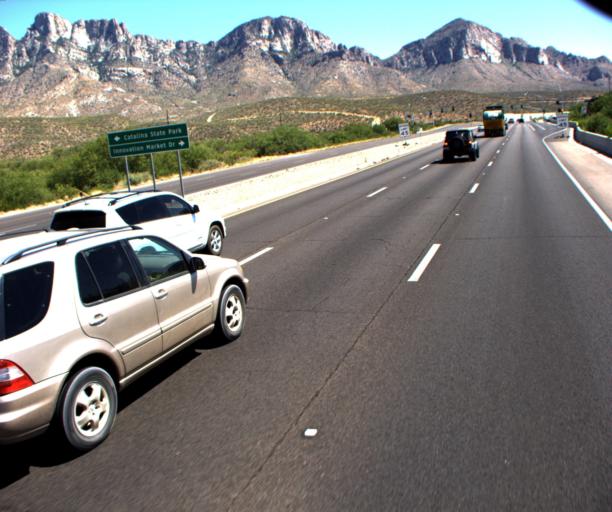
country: US
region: Arizona
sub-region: Pima County
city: Oro Valley
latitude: 32.4188
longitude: -110.9375
